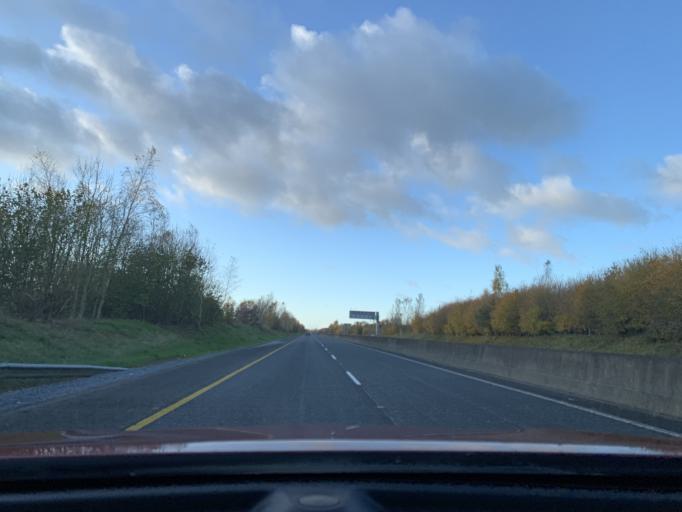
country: IE
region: Leinster
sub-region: An Iarmhi
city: Kinnegad
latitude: 53.4607
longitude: -7.1335
